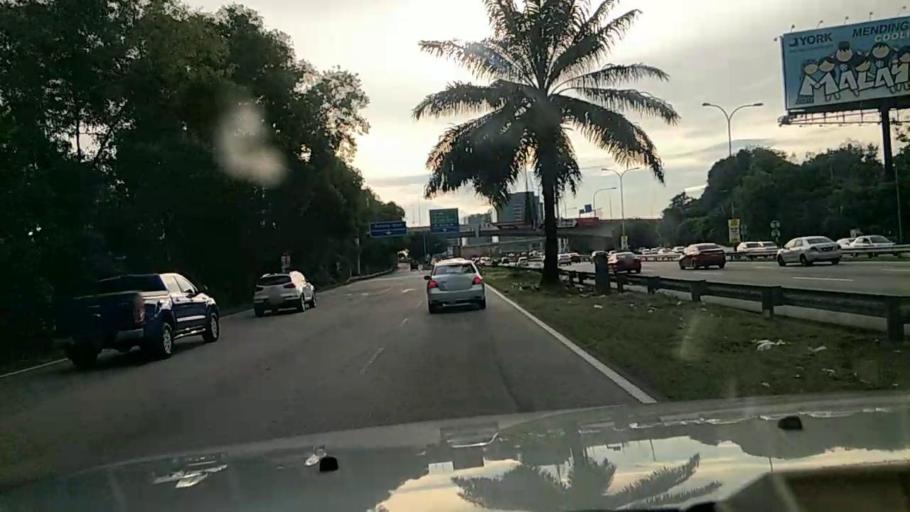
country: MY
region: Selangor
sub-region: Petaling
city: Petaling Jaya
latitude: 3.0840
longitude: 101.5959
